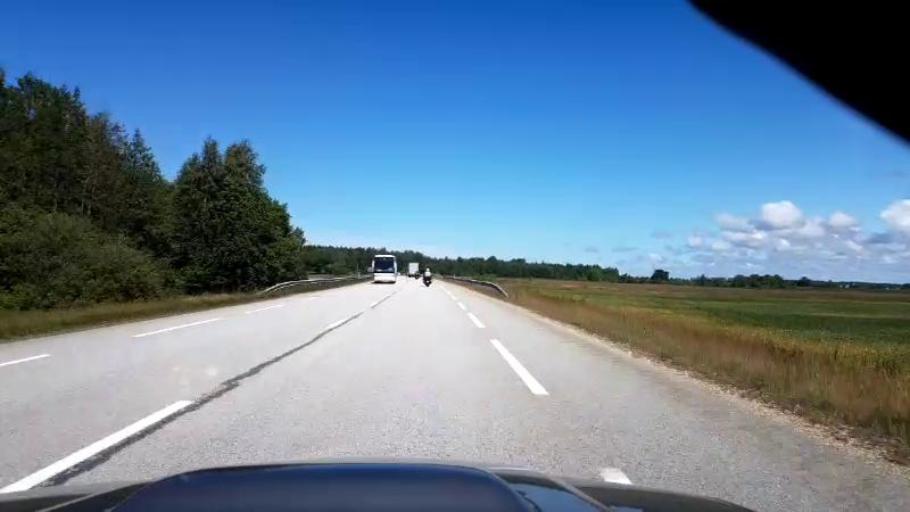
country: LV
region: Saulkrastu
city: Saulkrasti
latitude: 57.4138
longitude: 24.4307
